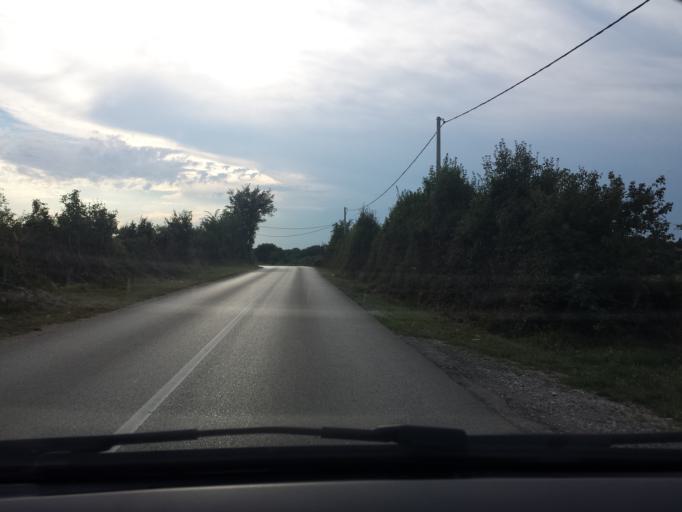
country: HR
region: Istarska
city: Galizana
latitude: 44.9067
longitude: 13.8544
